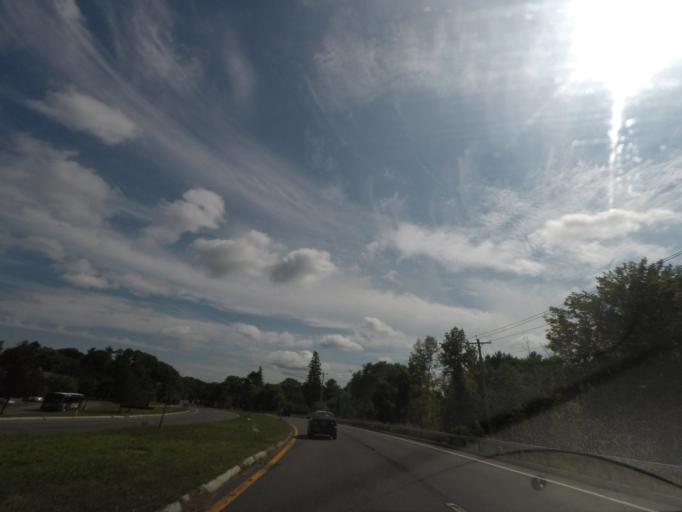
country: US
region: New York
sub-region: Albany County
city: Delmar
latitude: 42.6383
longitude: -73.8588
